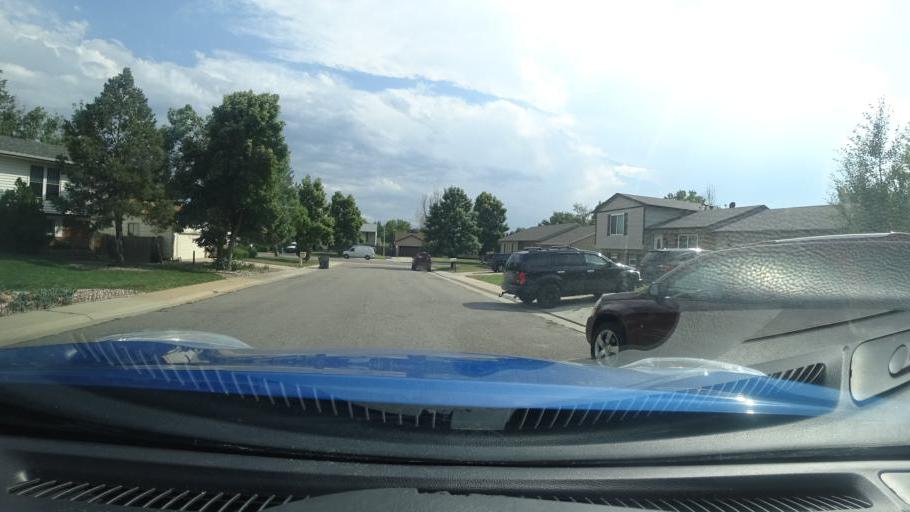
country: US
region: Colorado
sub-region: Adams County
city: Aurora
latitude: 39.6920
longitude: -104.7958
